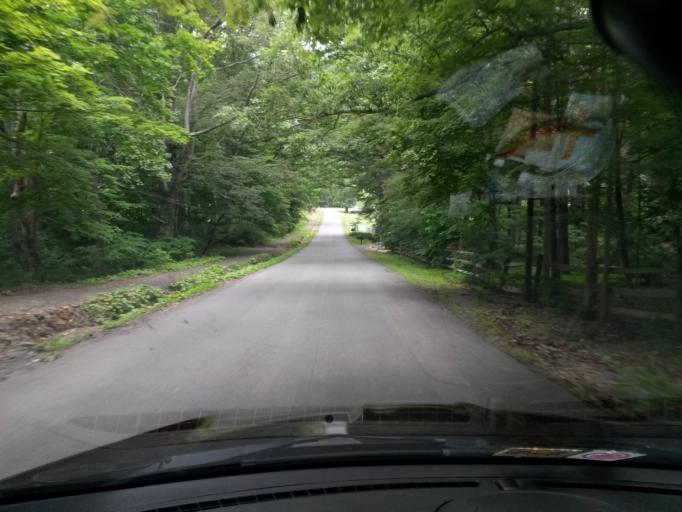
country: US
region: Virginia
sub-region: Bath County
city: Warm Springs
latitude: 38.0068
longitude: -79.8146
